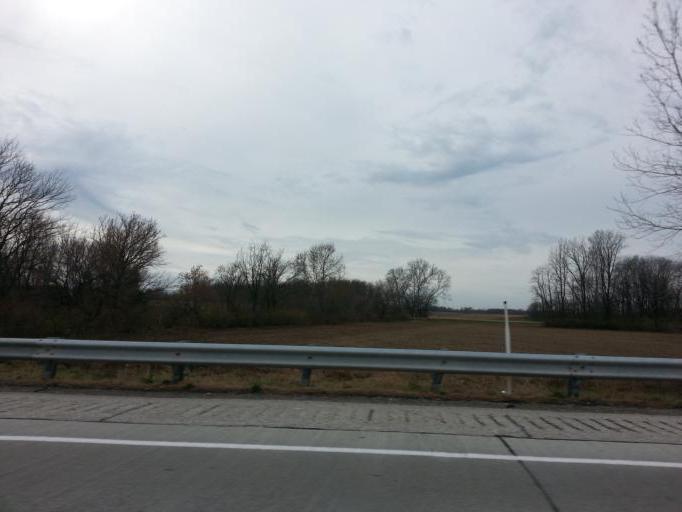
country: US
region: Indiana
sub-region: Decatur County
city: Greensburg
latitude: 39.3506
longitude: -85.4461
